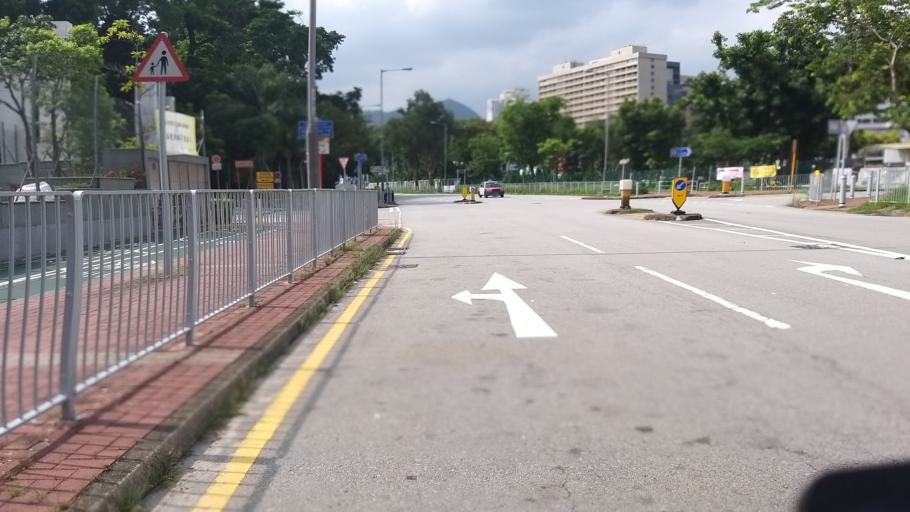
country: HK
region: Tuen Mun
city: Tuen Mun
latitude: 22.4063
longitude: 113.9748
